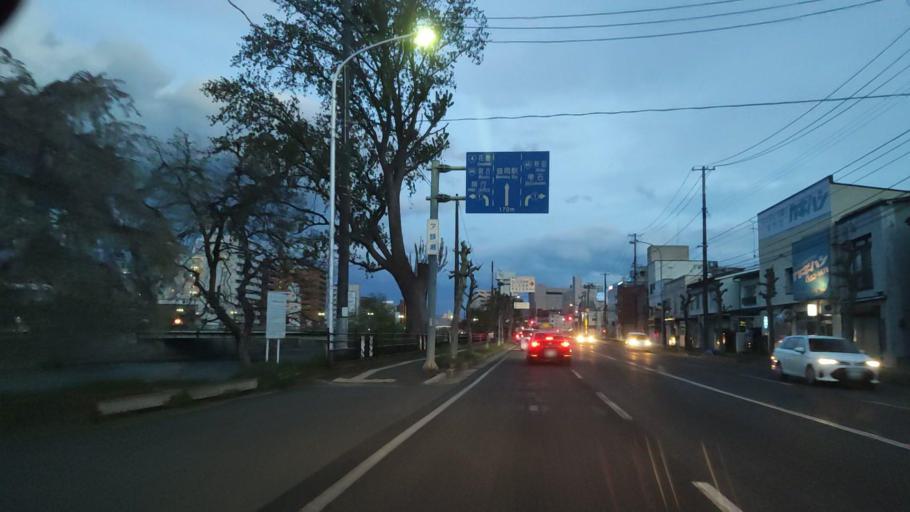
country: JP
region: Iwate
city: Morioka-shi
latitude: 39.7093
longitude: 141.1333
